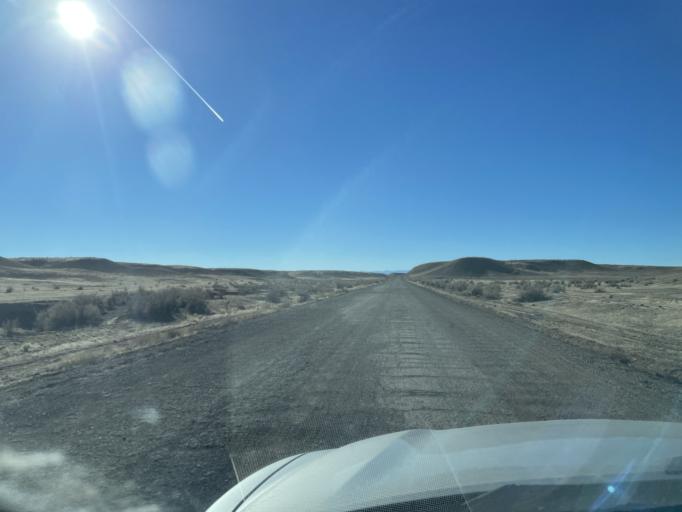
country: US
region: Colorado
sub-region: Mesa County
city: Loma
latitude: 39.2059
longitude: -109.0857
